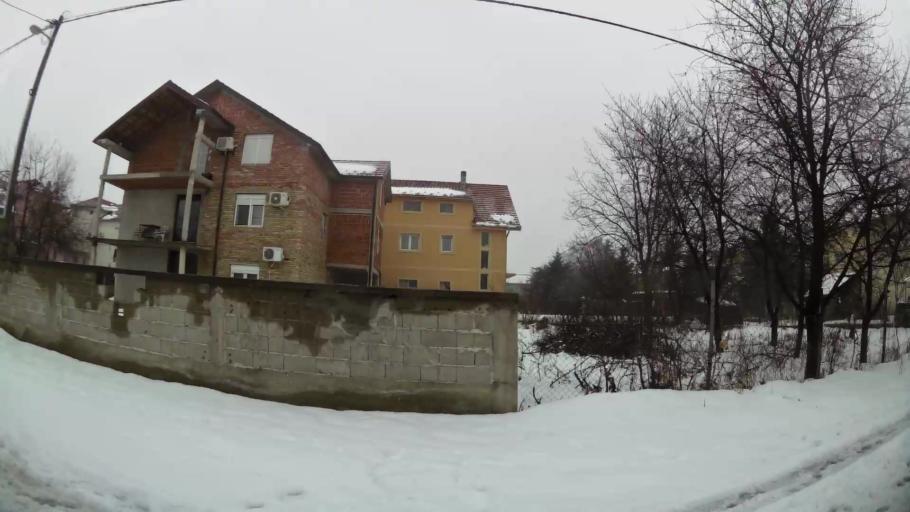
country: RS
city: Novi Banovci
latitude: 44.8749
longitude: 20.3165
